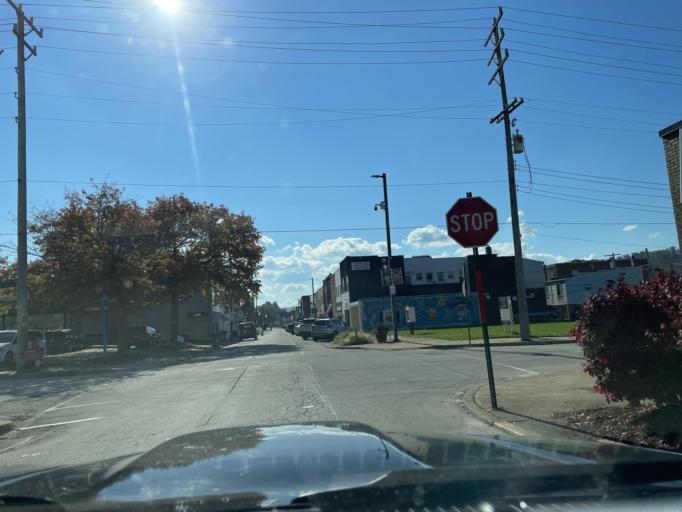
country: US
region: Pennsylvania
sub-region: Westmoreland County
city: Arnold
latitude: 40.5790
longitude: -79.7680
